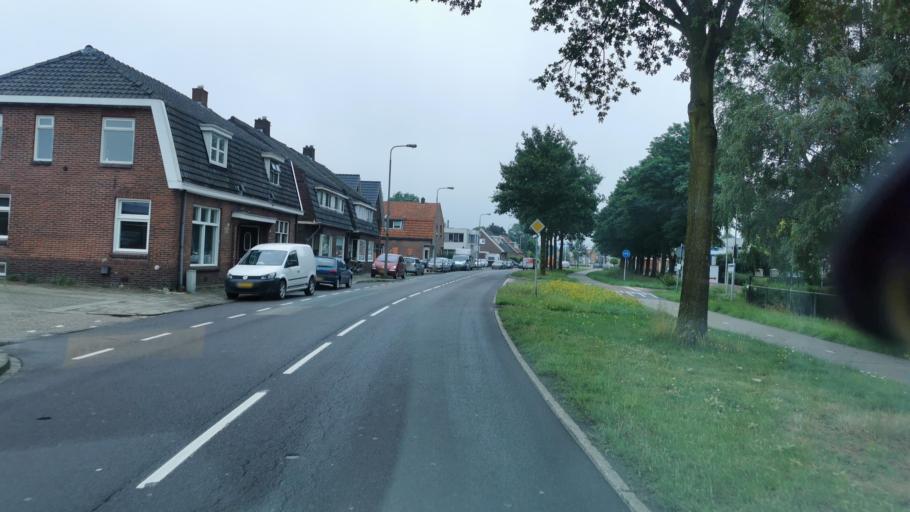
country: NL
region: Overijssel
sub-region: Gemeente Losser
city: Losser
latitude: 52.2498
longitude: 7.0092
